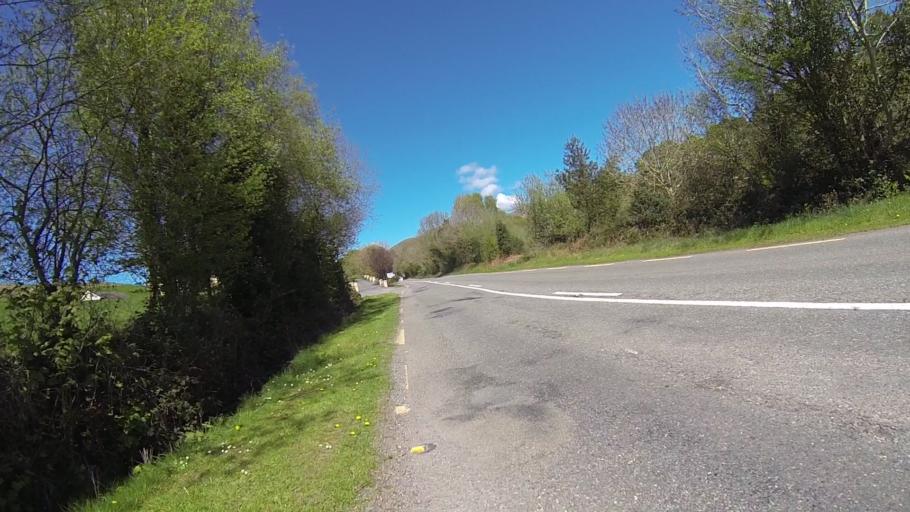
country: IE
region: Munster
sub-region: Ciarrai
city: Kenmare
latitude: 51.8917
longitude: -9.5996
